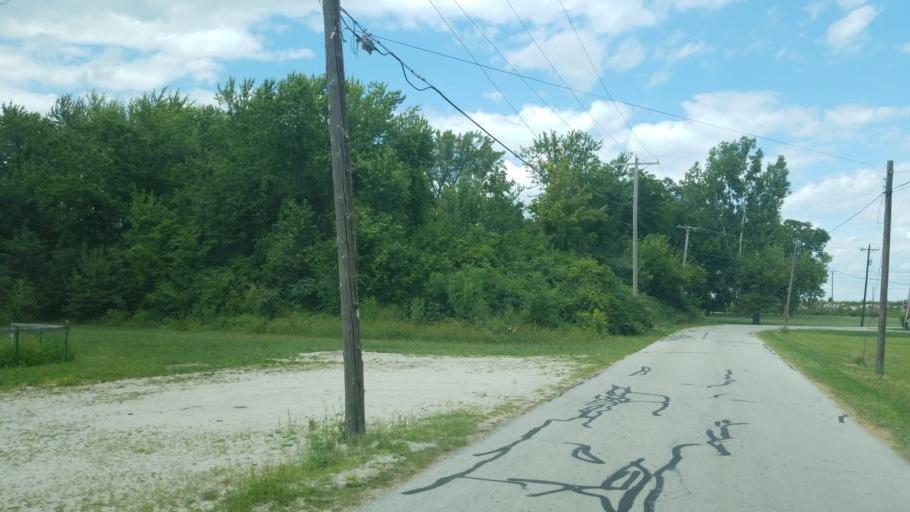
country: US
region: Ohio
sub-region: Lucas County
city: Curtice
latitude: 41.6677
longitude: -83.2739
